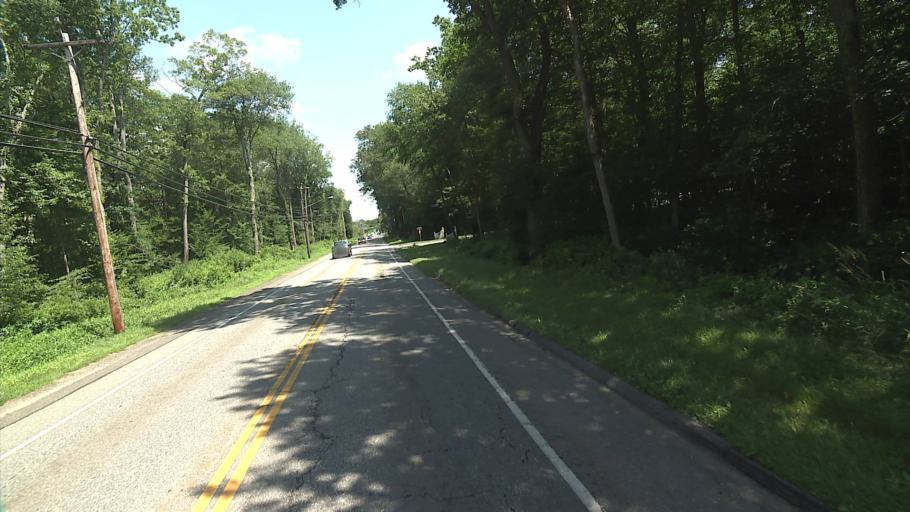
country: US
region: Connecticut
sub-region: Middlesex County
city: Old Saybrook
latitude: 41.3183
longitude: -72.3805
